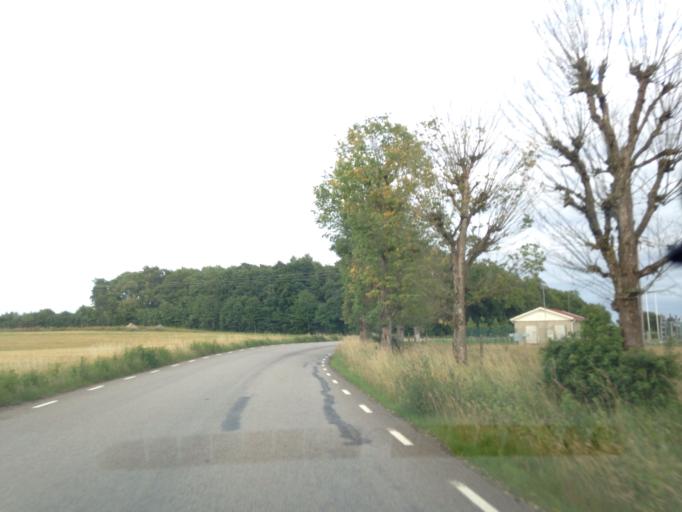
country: SE
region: Halland
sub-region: Varbergs Kommun
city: Tvaaker
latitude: 57.1153
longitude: 12.4015
